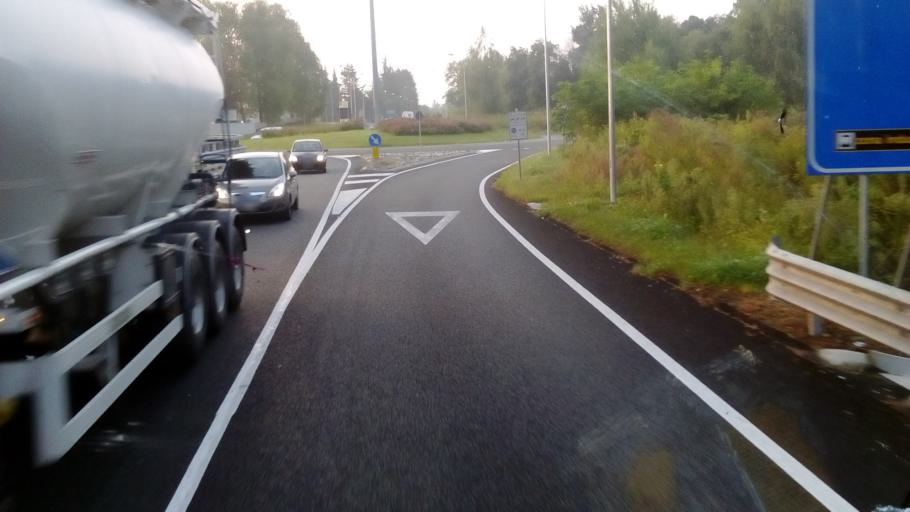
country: IT
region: Piedmont
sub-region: Provincia di Novara
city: Varallo Pombia
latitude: 45.6726
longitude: 8.6147
